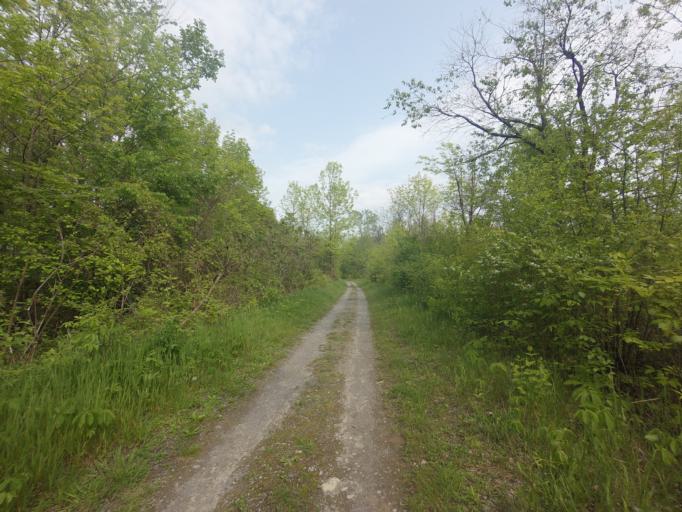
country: CA
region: Ontario
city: Kingston
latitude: 44.4097
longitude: -76.6173
